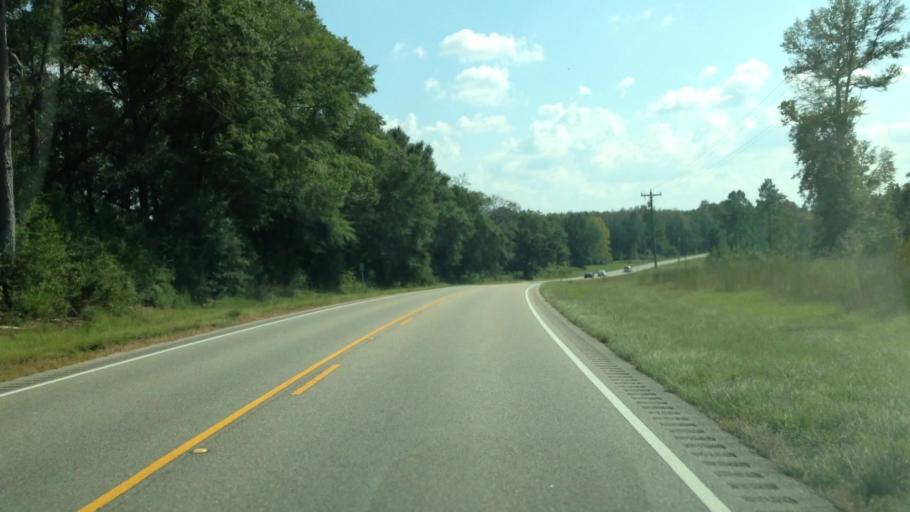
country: US
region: Alabama
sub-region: Covington County
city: Florala
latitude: 31.0662
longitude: -86.5745
